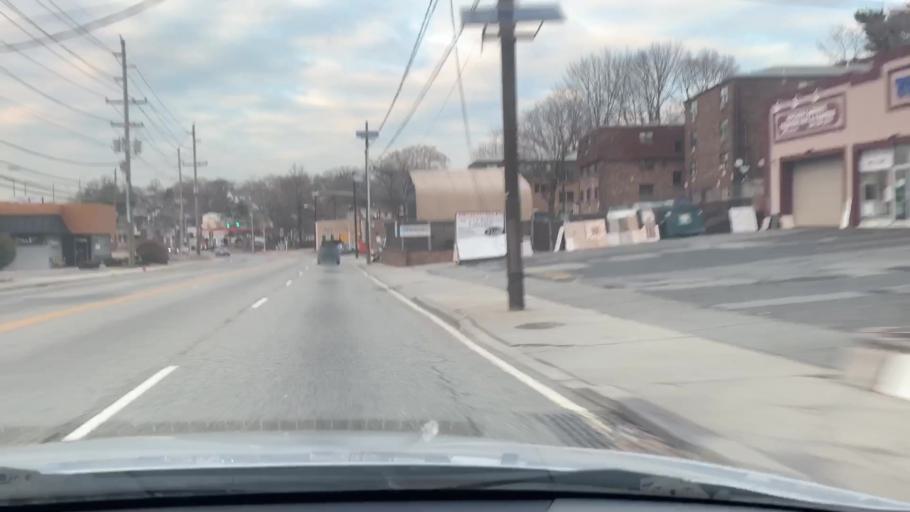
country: US
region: New Jersey
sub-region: Bergen County
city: Ridgefield
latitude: 40.8229
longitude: -74.0086
